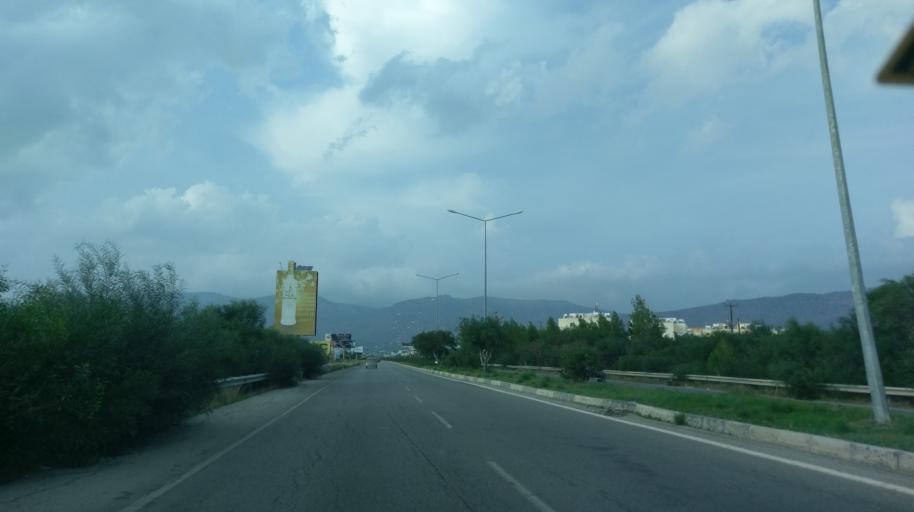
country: CY
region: Keryneia
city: Kyrenia
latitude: 35.2568
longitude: 33.2992
